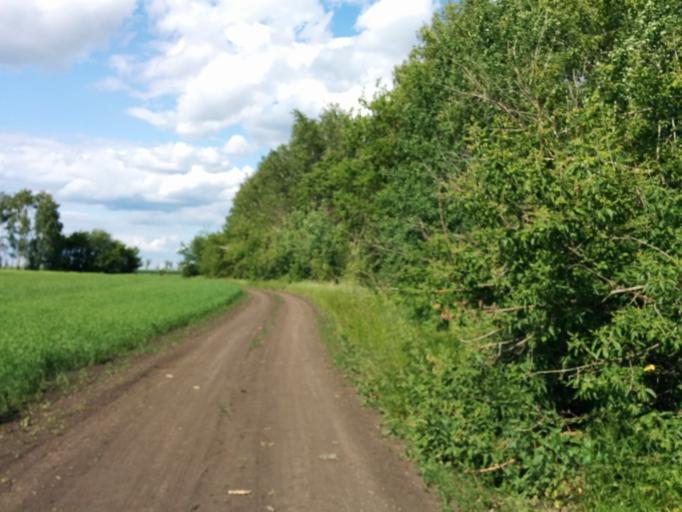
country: RU
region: Tambov
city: Tambov
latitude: 52.8045
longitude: 41.3908
